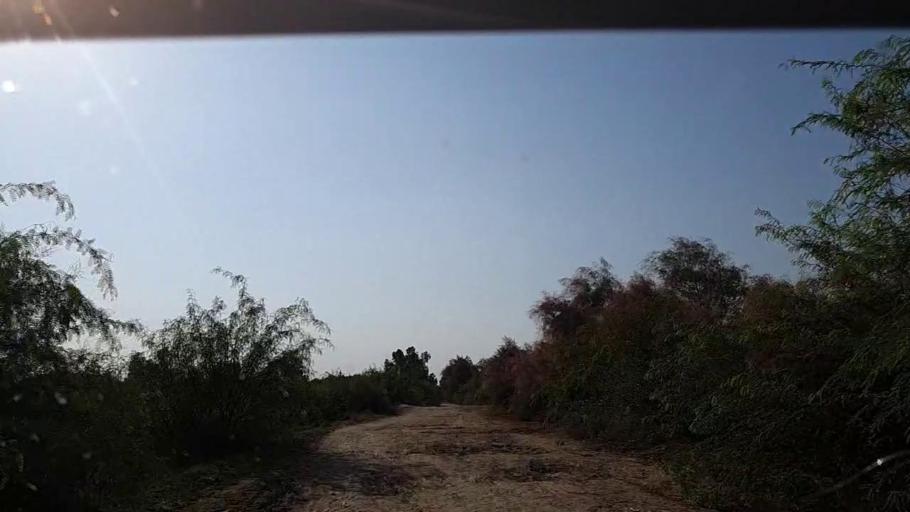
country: PK
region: Sindh
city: Adilpur
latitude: 27.9018
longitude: 69.2300
